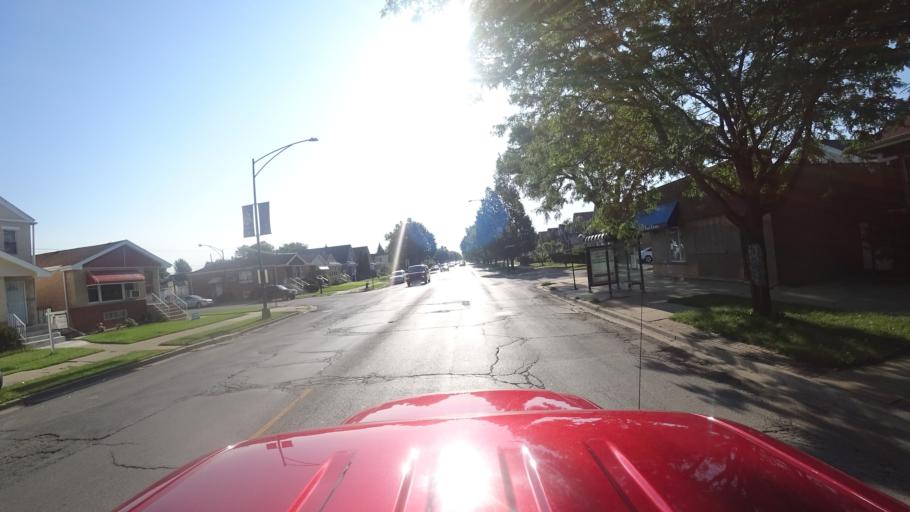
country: US
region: Illinois
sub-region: Cook County
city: Hometown
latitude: 41.7932
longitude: -87.7212
